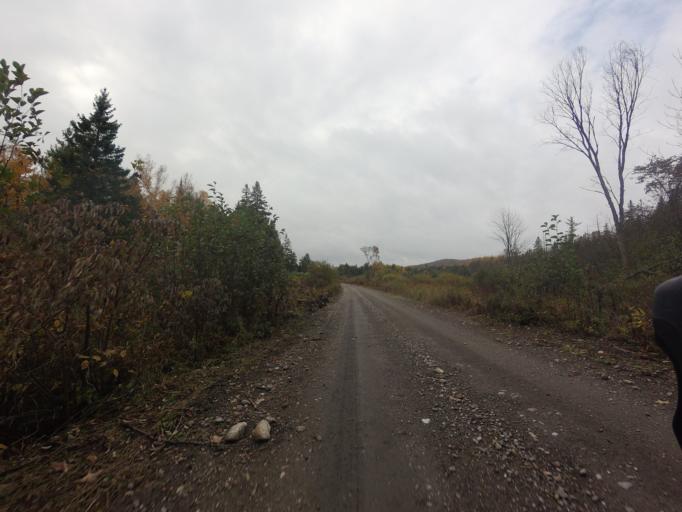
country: CA
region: Ontario
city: Renfrew
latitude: 45.1637
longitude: -76.6835
